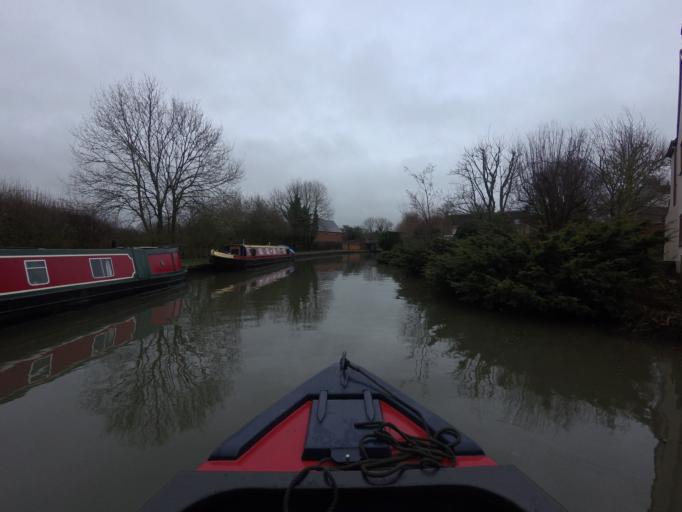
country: GB
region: England
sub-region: Northamptonshire
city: Long Buckby
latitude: 52.2840
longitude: -1.1047
